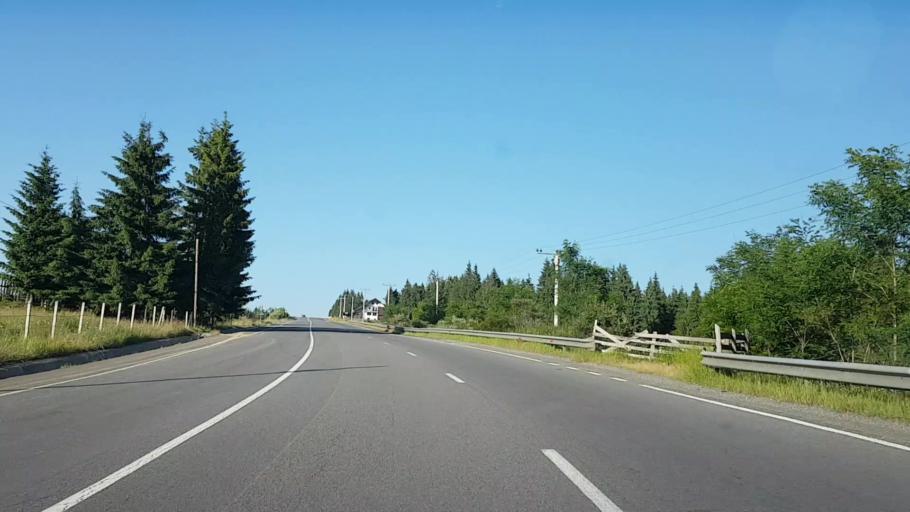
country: RO
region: Bistrita-Nasaud
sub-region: Comuna Lunca Ilvei
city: Lunca Ilvei
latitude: 47.2303
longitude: 24.9799
